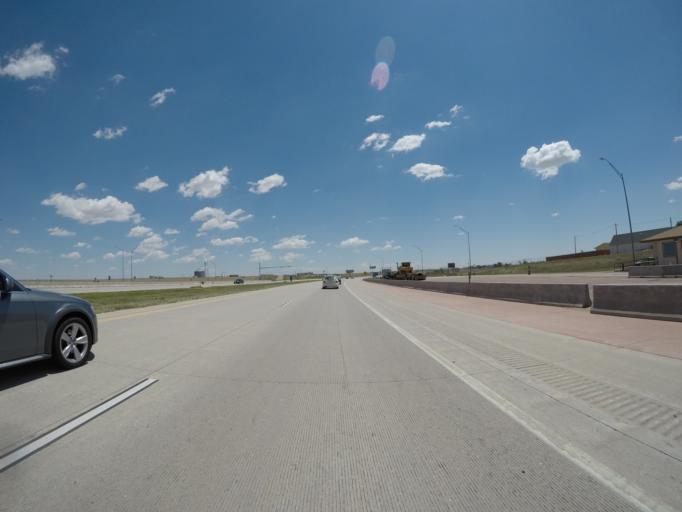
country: US
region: Colorado
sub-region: Lincoln County
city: Limon
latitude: 39.2732
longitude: -103.6857
